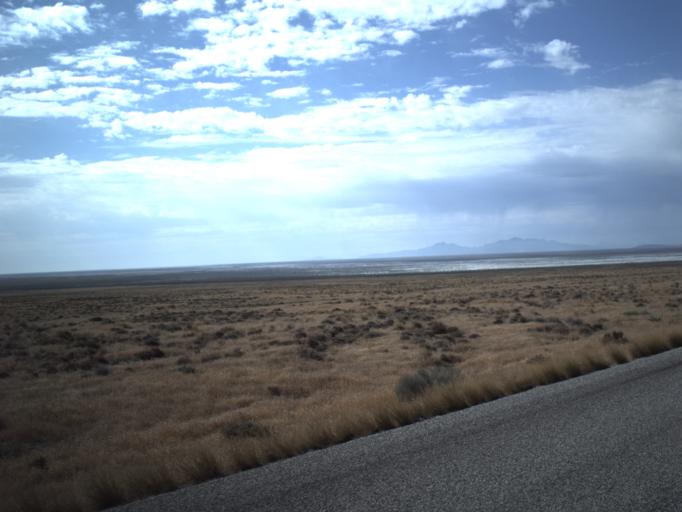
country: US
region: Utah
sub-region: Tooele County
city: Wendover
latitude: 41.4832
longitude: -113.6269
